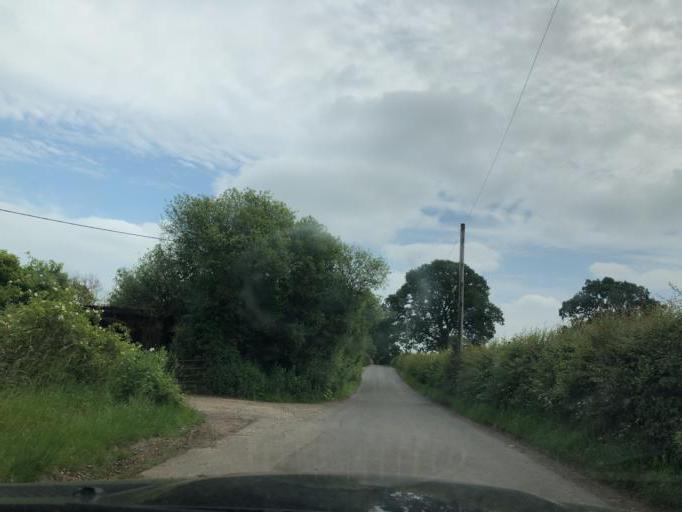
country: GB
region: England
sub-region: Warwickshire
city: Wroxall
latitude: 52.3355
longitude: -1.6421
